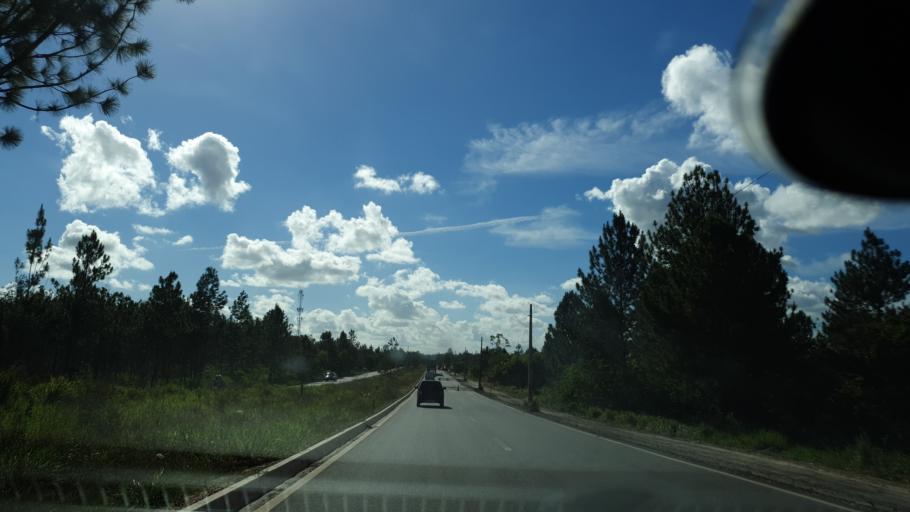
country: BR
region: Bahia
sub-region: Camacari
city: Camacari
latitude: -12.6825
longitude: -38.2936
